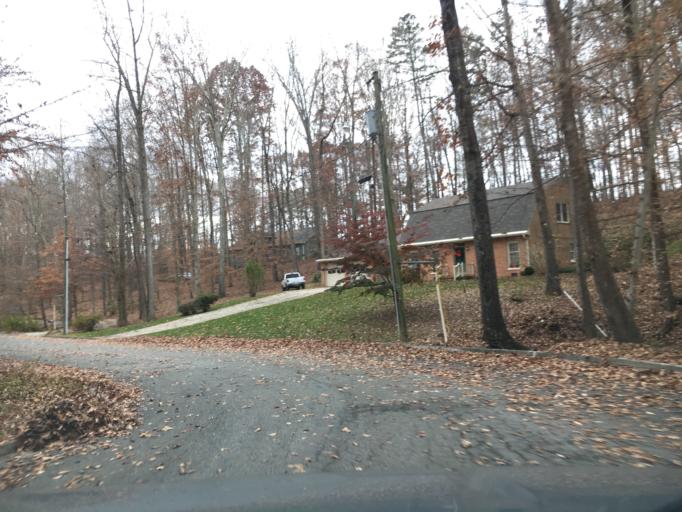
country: US
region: Virginia
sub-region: Halifax County
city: South Boston
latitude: 36.7272
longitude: -78.9127
